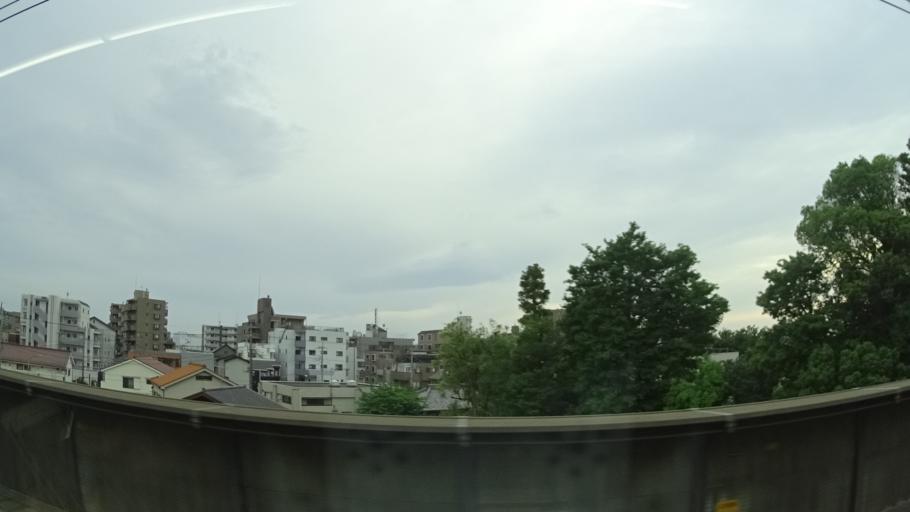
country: JP
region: Saitama
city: Shimotoda
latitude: 35.8127
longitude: 139.6724
